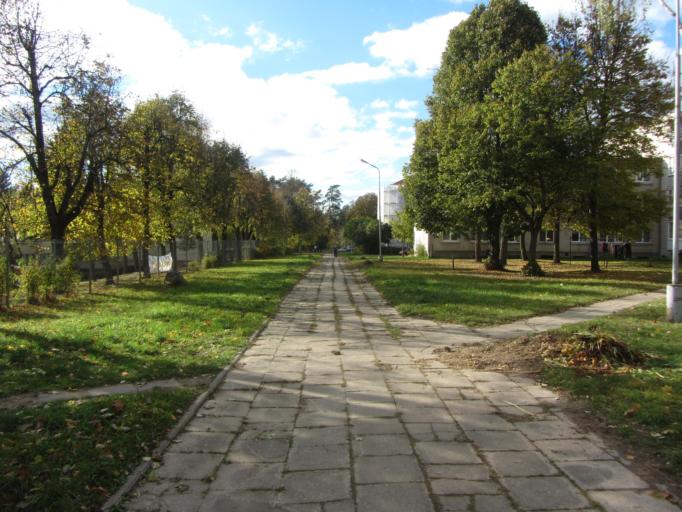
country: LT
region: Vilnius County
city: Lazdynai
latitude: 54.6693
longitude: 25.2180
